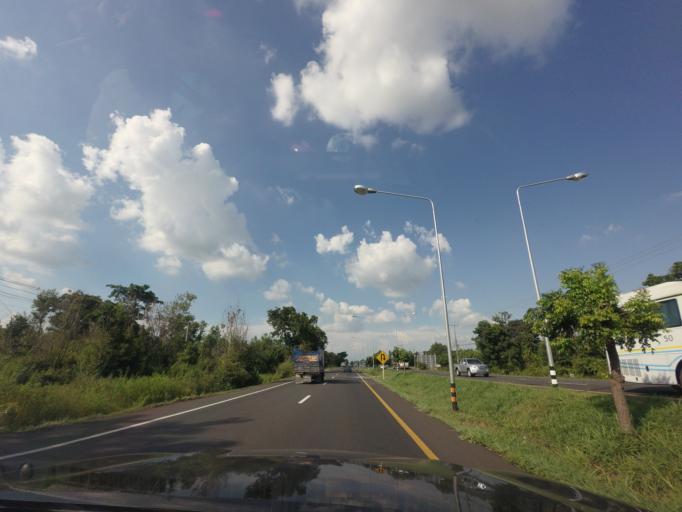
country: TH
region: Nakhon Ratchasima
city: Bua Lai
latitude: 15.7018
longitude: 102.5844
